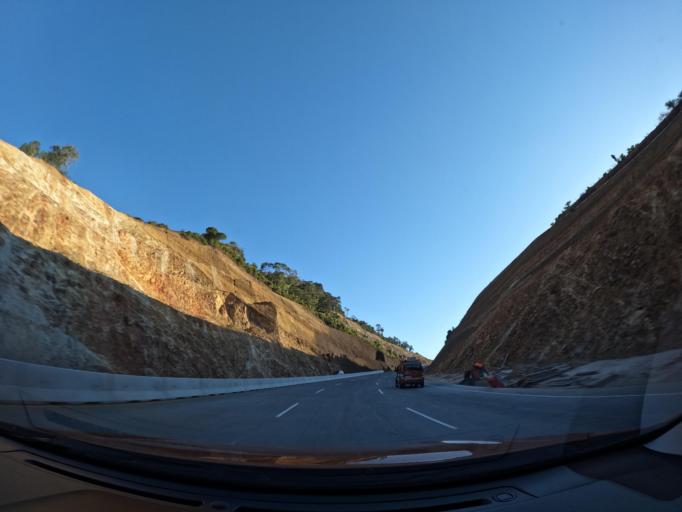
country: GT
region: Guatemala
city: Villa Canales
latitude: 14.4901
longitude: -90.4989
